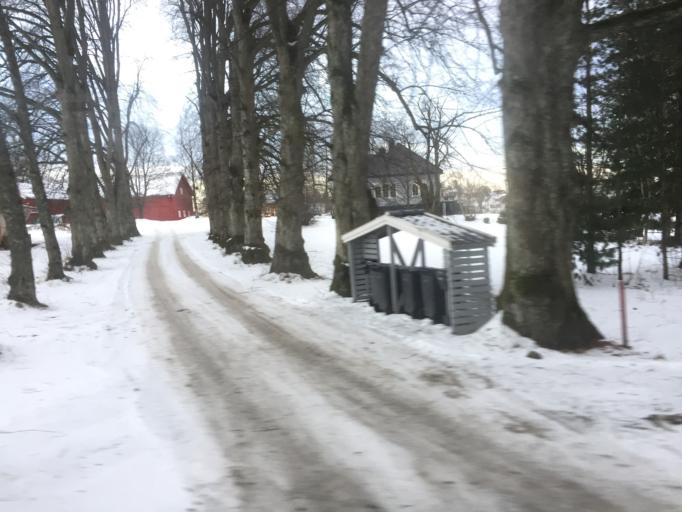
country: NO
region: Akershus
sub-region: Frogn
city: Drobak
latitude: 59.6866
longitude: 10.6644
